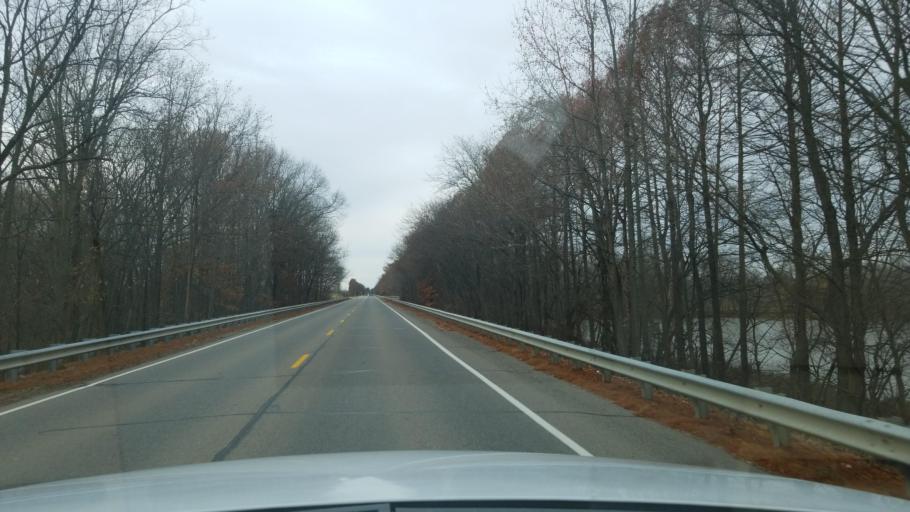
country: US
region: Indiana
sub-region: Posey County
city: Mount Vernon
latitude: 37.9290
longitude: -87.9786
